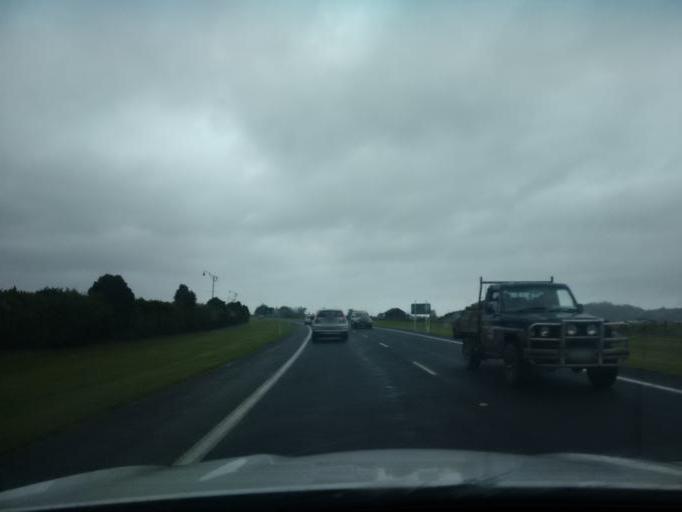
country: NZ
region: Waikato
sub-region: Thames-Coromandel District
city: Whitianga
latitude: -36.8319
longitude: 175.6813
